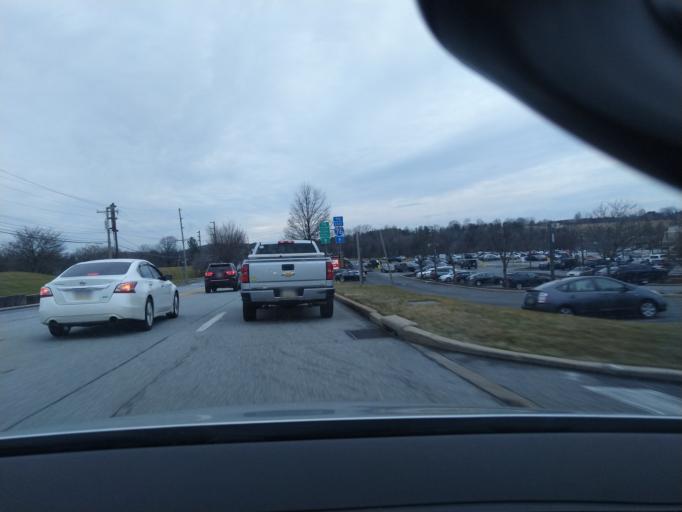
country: US
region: Pennsylvania
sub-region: Montgomery County
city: King of Prussia
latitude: 40.0951
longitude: -75.4140
